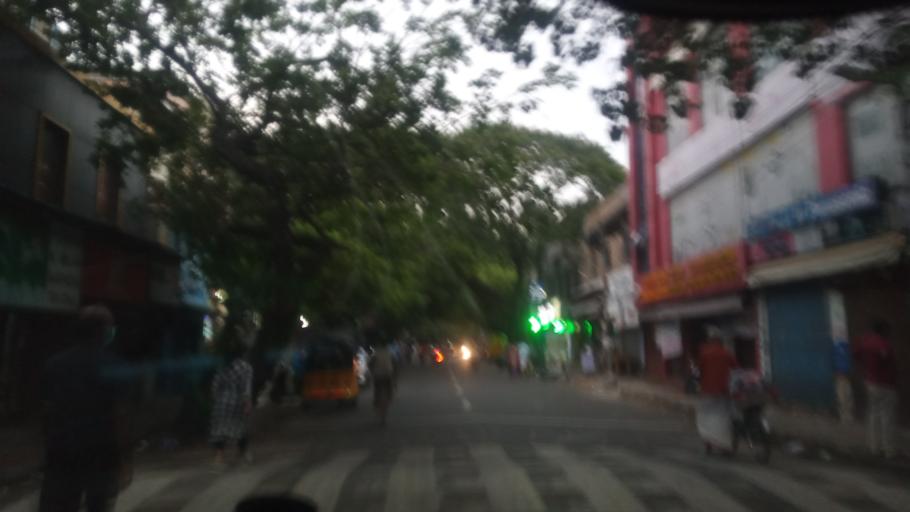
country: IN
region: Tamil Nadu
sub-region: Chennai
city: Chetput
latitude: 13.0410
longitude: 80.2216
